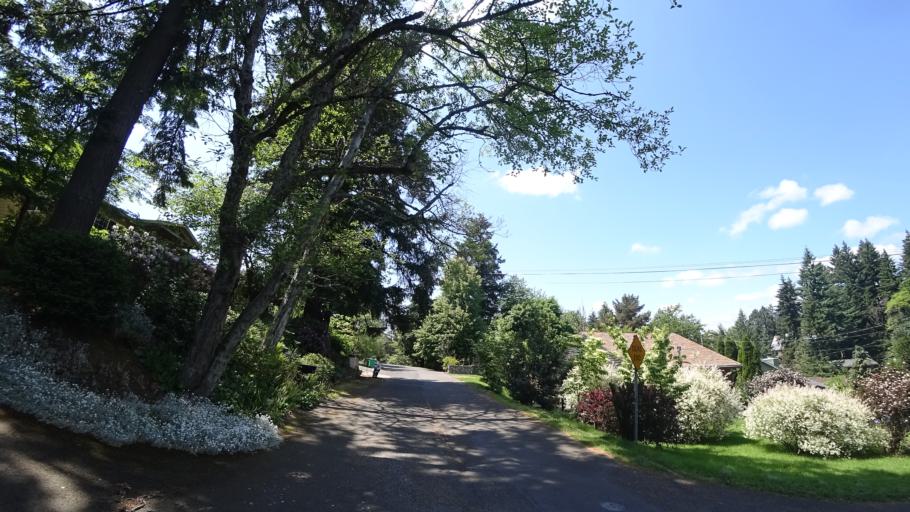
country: US
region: Oregon
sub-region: Multnomah County
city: Portland
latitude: 45.4711
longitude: -122.6960
